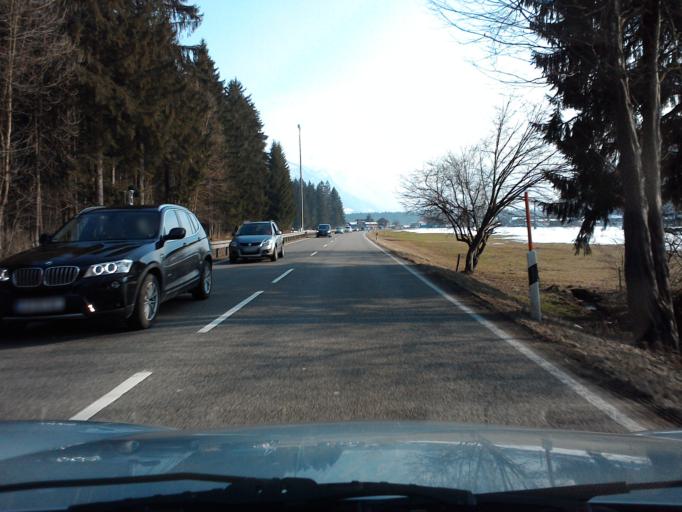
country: DE
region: Bavaria
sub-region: Swabia
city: Oberstdorf
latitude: 47.4449
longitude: 10.2739
